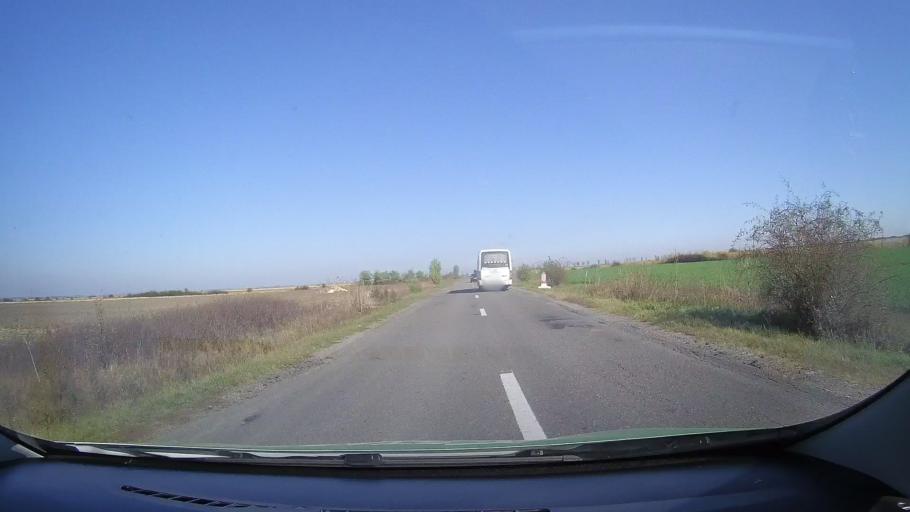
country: RO
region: Satu Mare
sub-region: Comuna Cauas
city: Cauas
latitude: 47.5853
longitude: 22.5473
